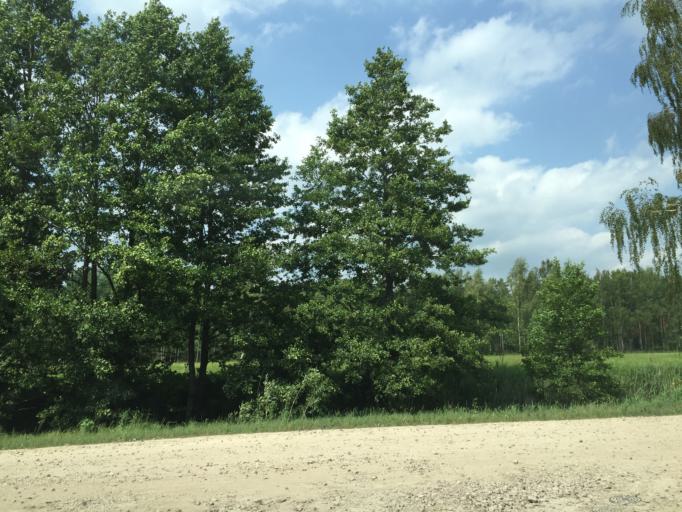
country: LV
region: Olaine
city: Olaine
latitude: 56.7778
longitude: 23.9211
